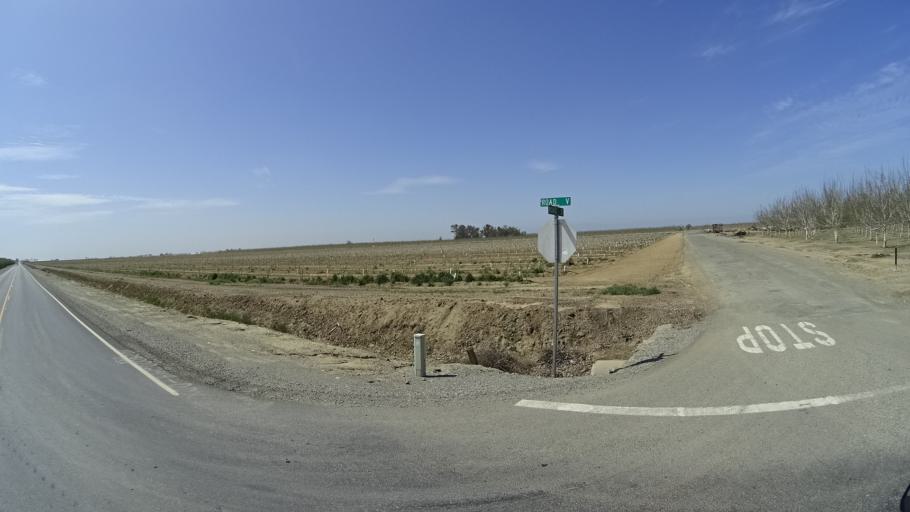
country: US
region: California
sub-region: Glenn County
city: Hamilton City
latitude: 39.6380
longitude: -122.0649
